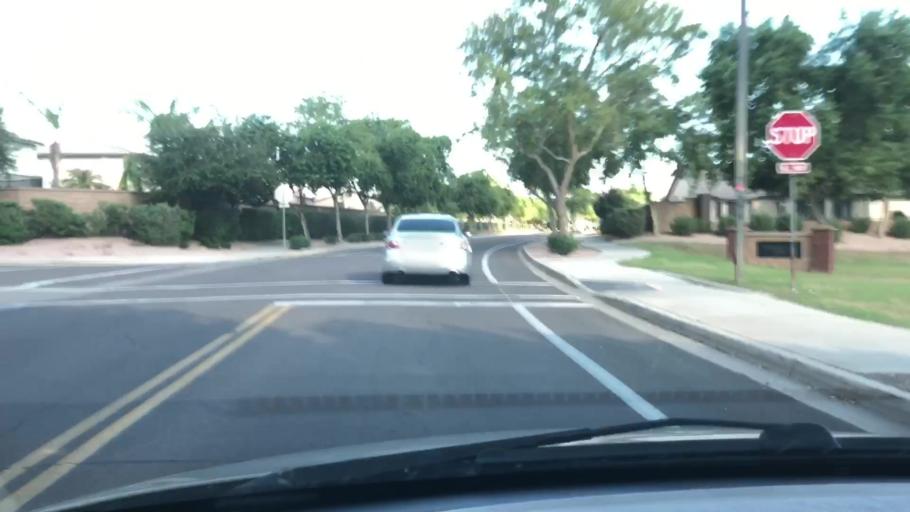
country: US
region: Arizona
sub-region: Maricopa County
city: Queen Creek
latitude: 33.2673
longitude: -111.7145
